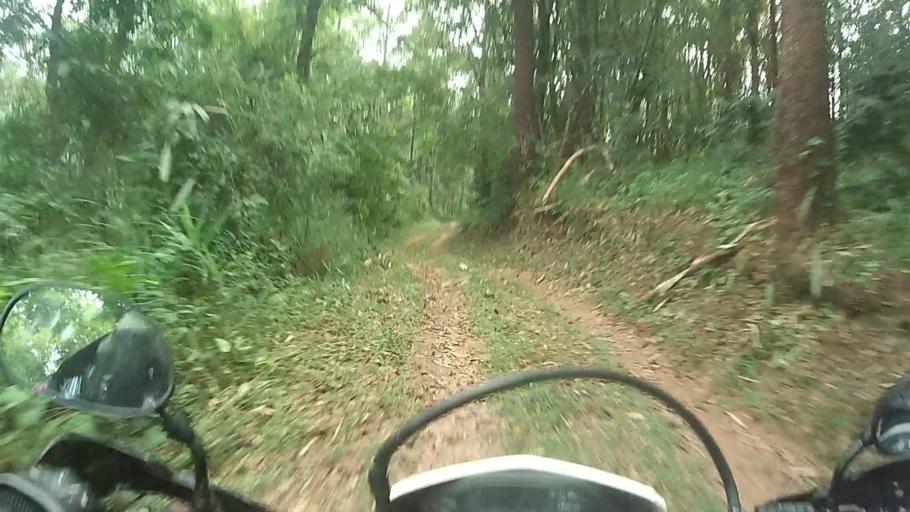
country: TH
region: Lampang
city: Mueang Pan
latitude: 18.8167
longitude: 99.3869
